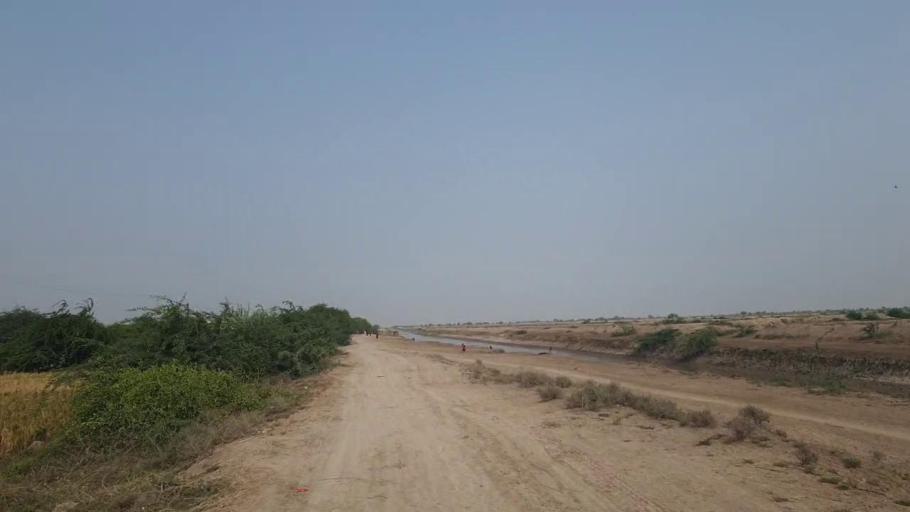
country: PK
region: Sindh
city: Badin
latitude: 24.7161
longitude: 68.7716
